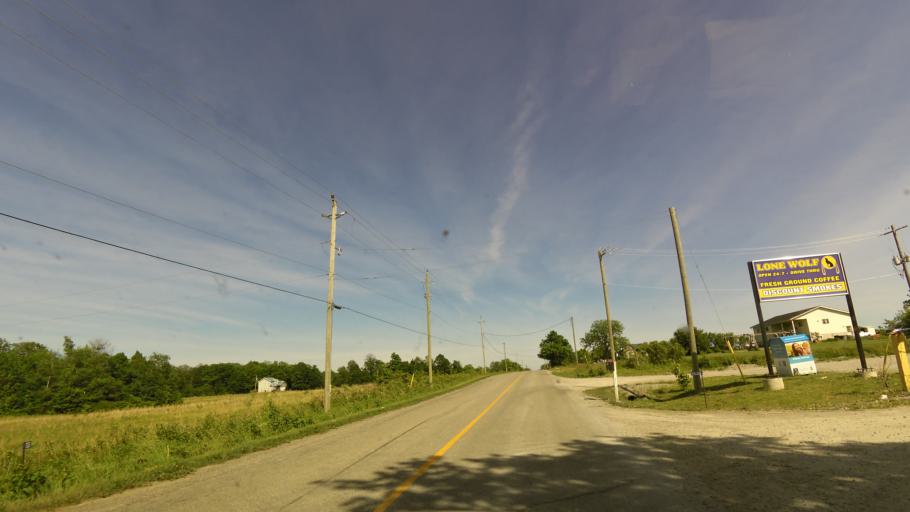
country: CA
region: Ontario
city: Ancaster
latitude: 43.0501
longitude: -80.0115
